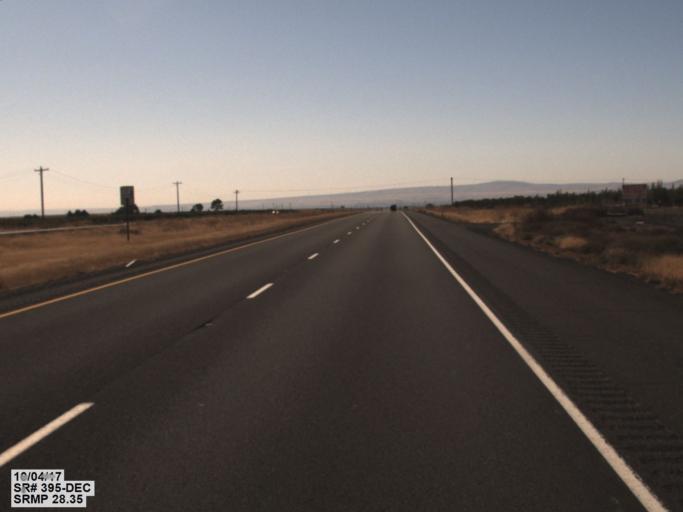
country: US
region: Washington
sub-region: Franklin County
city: Pasco
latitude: 46.3320
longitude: -119.0932
